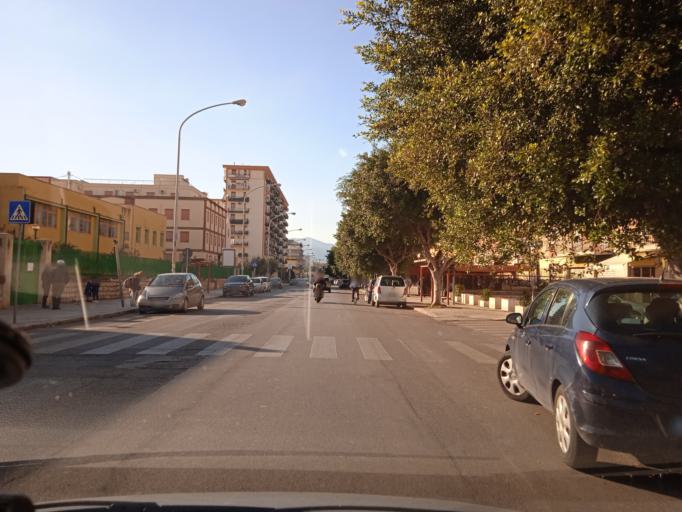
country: IT
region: Sicily
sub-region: Palermo
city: Ciaculli
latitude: 38.1040
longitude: 13.3844
